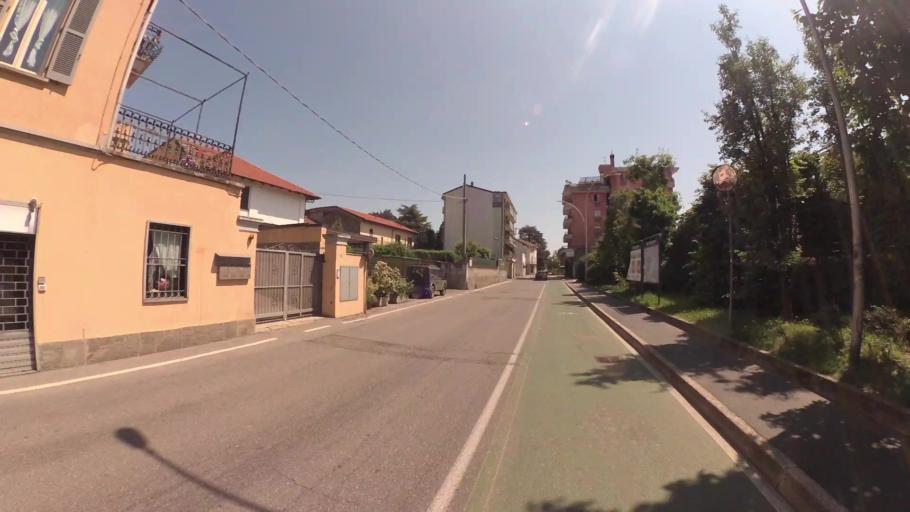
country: IT
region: Lombardy
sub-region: Provincia di Varese
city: Tradate
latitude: 45.7113
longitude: 8.9061
